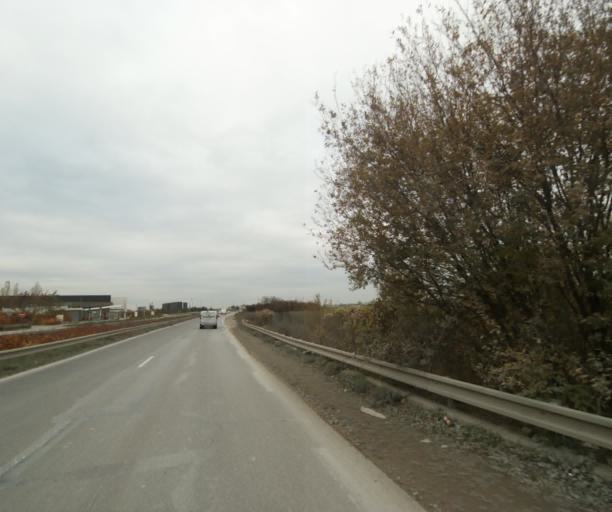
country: FR
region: Ile-de-France
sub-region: Departement de Seine-Saint-Denis
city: Le Blanc-Mesnil
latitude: 48.9659
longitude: 2.4679
